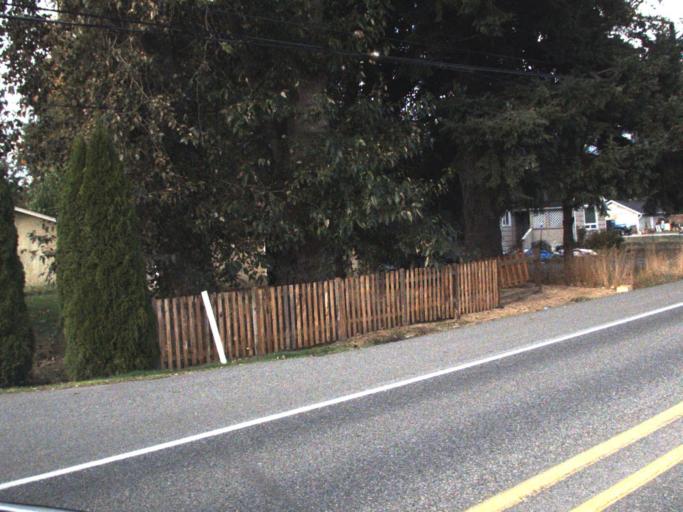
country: US
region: Washington
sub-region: Skagit County
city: Burlington
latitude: 48.4895
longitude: -122.2885
